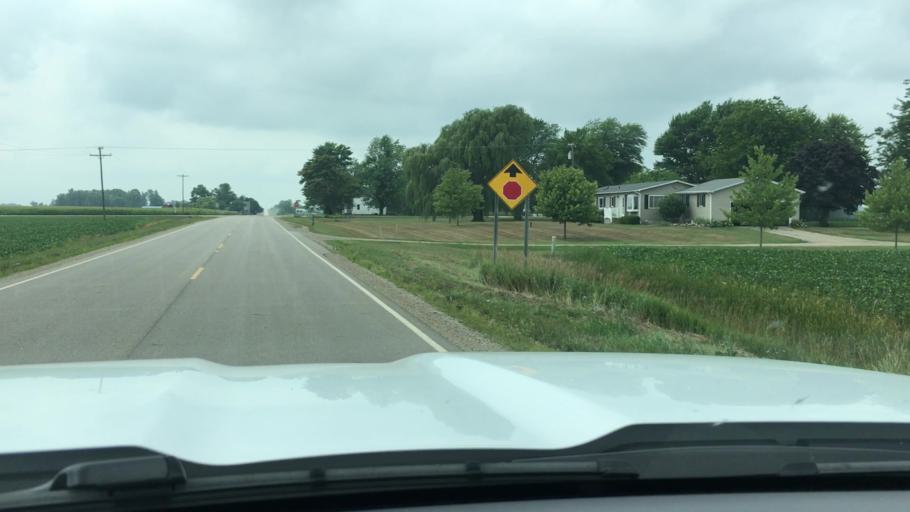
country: US
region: Michigan
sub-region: Sanilac County
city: Marlette
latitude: 43.3586
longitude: -83.0035
